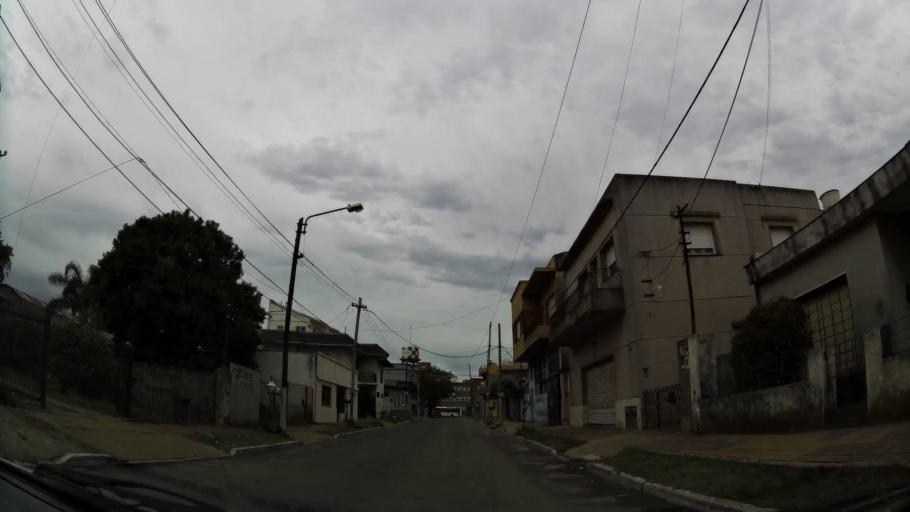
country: AR
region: Buenos Aires
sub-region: Partido de Quilmes
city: Quilmes
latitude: -34.7518
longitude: -58.2146
